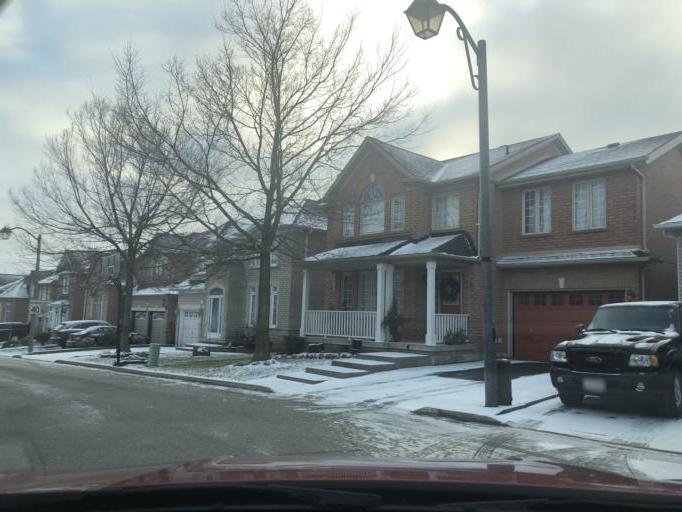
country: CA
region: Ontario
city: Markham
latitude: 43.8673
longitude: -79.2341
